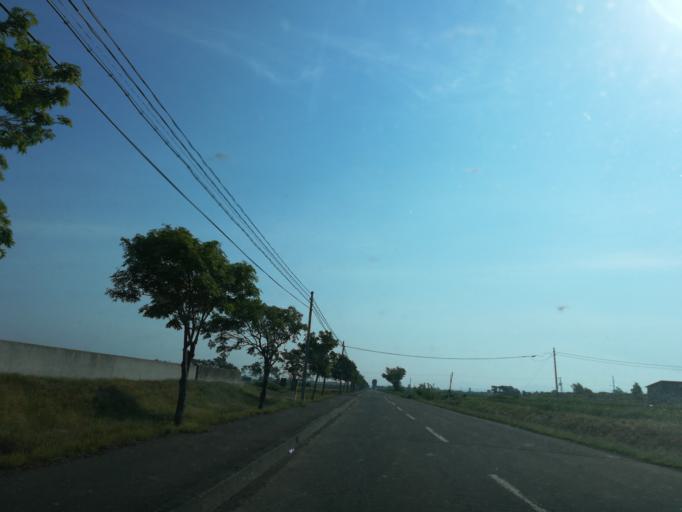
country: JP
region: Hokkaido
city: Iwamizawa
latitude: 43.1635
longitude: 141.6916
